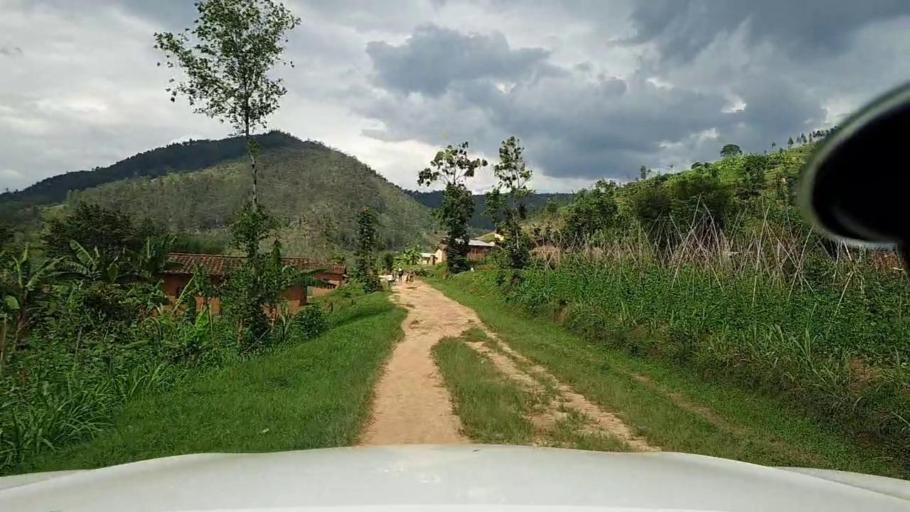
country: RW
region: Southern Province
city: Gitarama
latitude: -1.8196
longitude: 29.8003
